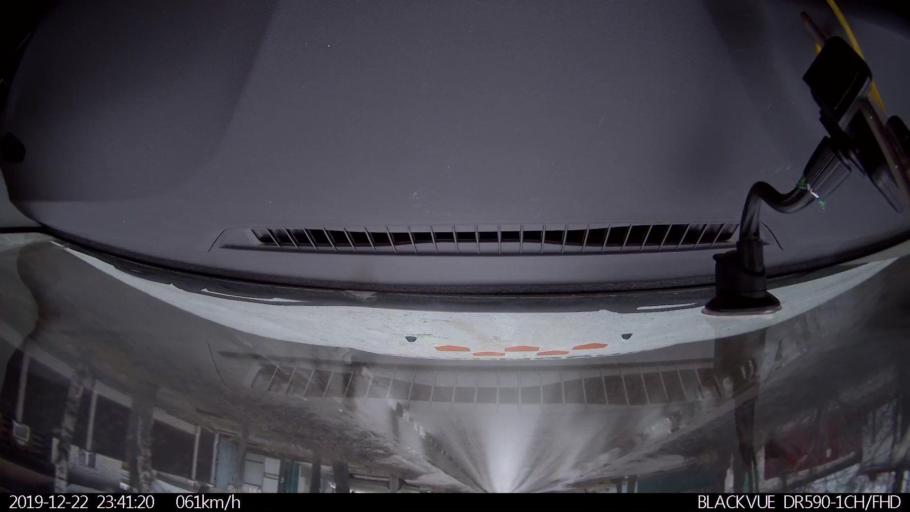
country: RU
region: Nizjnij Novgorod
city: Nizhniy Novgorod
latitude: 56.2845
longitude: 43.9114
